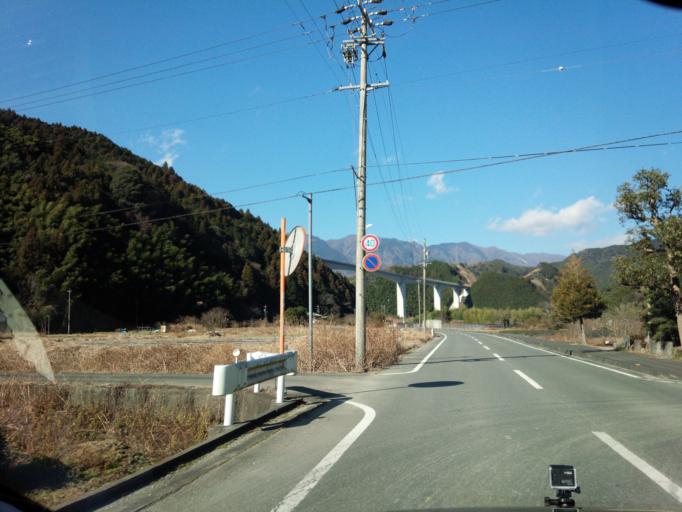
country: JP
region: Shizuoka
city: Shizuoka-shi
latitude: 35.1142
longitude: 138.4607
